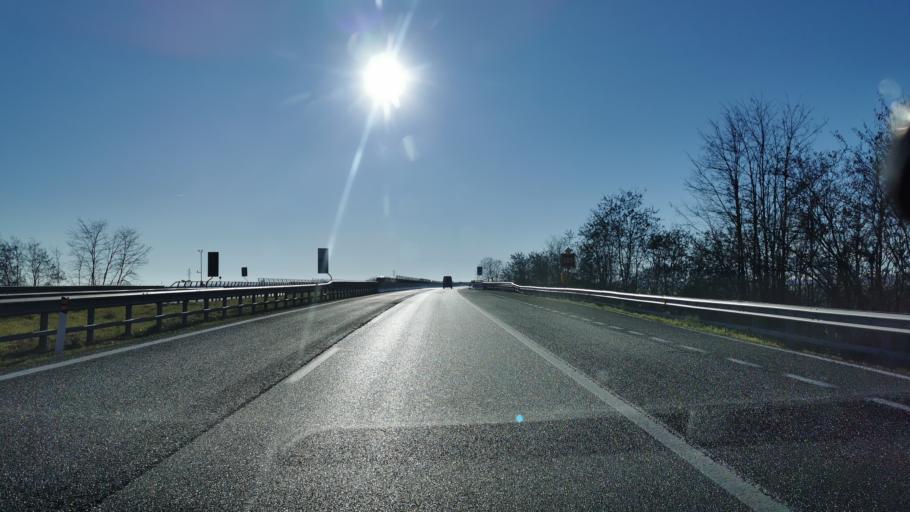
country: IT
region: Piedmont
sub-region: Provincia di Torino
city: Villastellone
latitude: 44.9081
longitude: 7.7413
